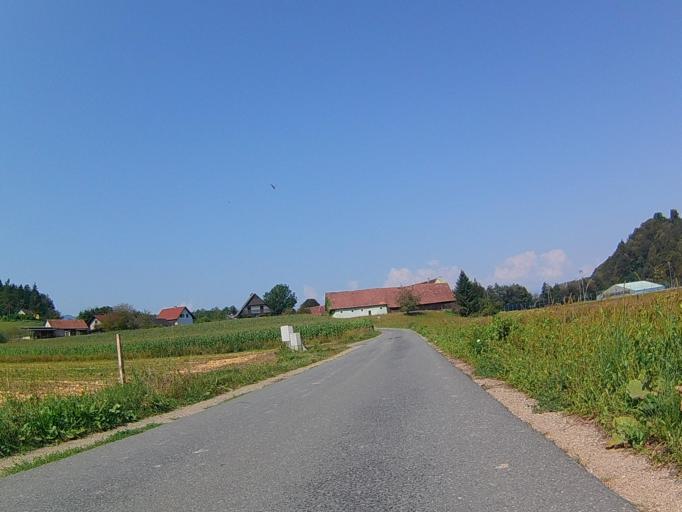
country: AT
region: Styria
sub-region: Politischer Bezirk Leibnitz
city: Arnfels
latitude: 46.6723
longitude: 15.4106
